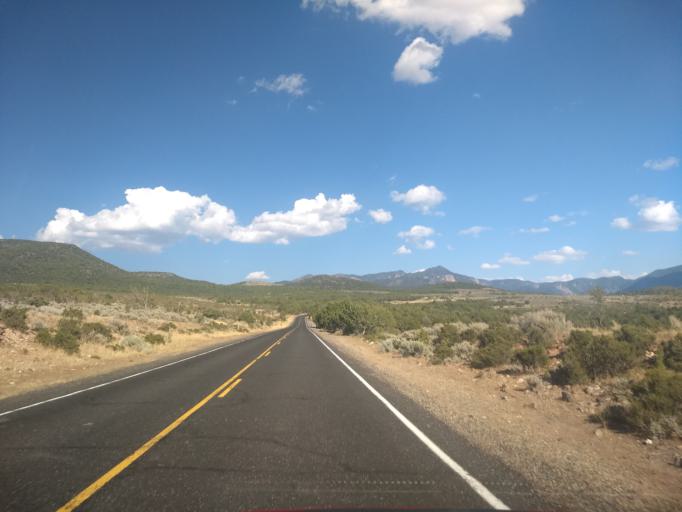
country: US
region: Utah
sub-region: Washington County
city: Enterprise
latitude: 37.4183
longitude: -113.5525
